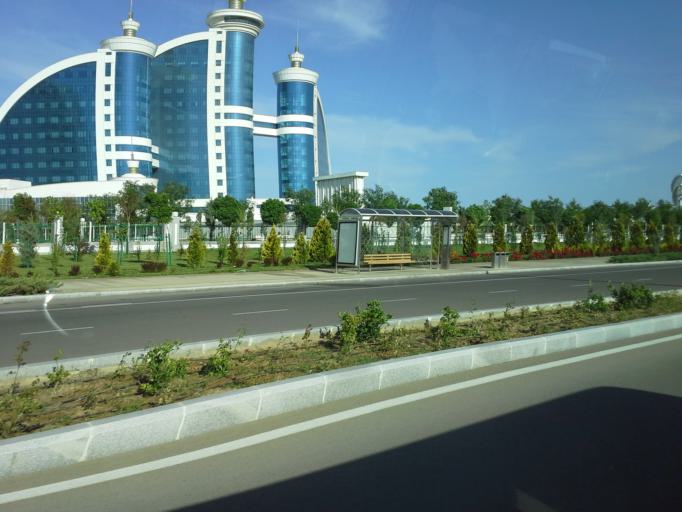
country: TM
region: Balkan
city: Turkmenbasy
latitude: 39.9802
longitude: 52.8271
